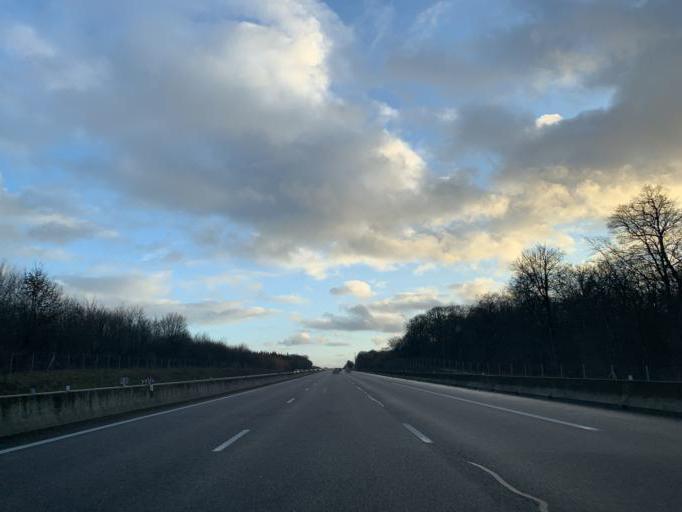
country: FR
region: Bourgogne
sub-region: Departement de la Cote-d'Or
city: Selongey
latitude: 47.6544
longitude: 5.1763
